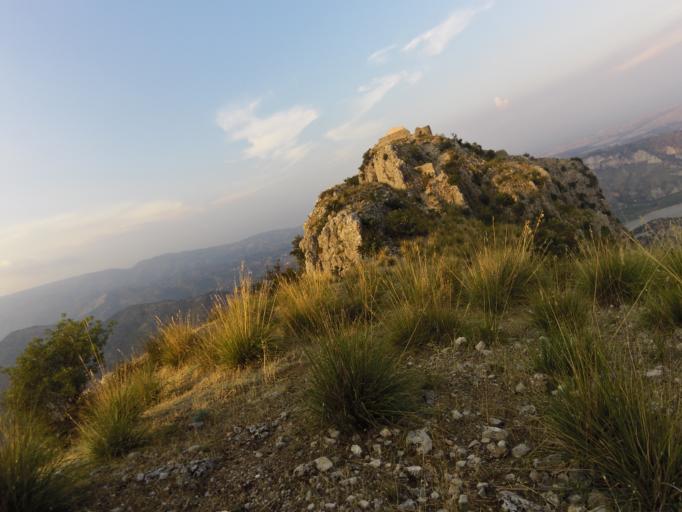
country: IT
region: Calabria
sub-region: Provincia di Reggio Calabria
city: Stilo
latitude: 38.4795
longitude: 16.4612
